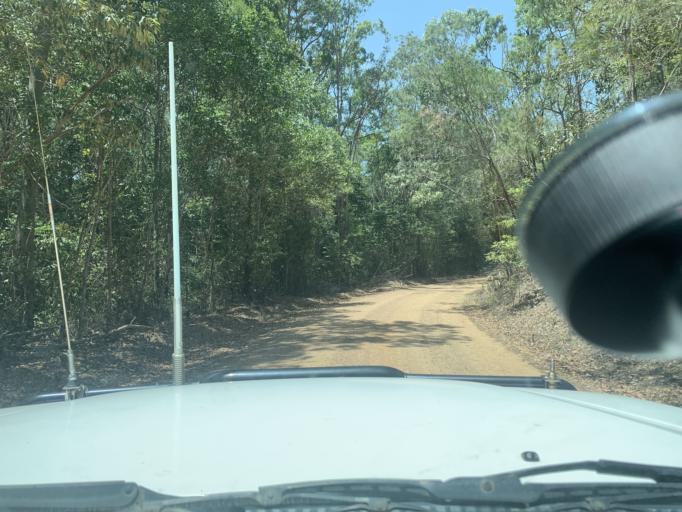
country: AU
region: Queensland
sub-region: Cairns
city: Redlynch
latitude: -16.9238
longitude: 145.6037
